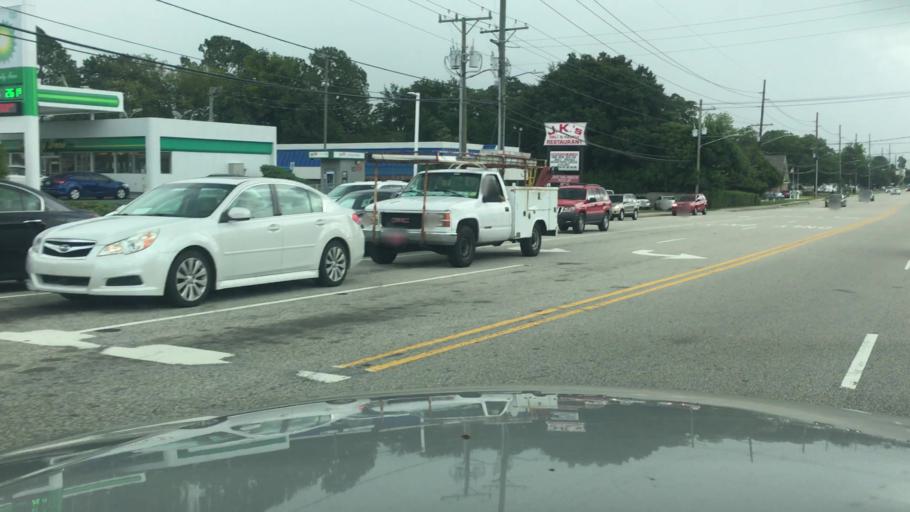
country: US
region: North Carolina
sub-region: Cumberland County
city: Fayetteville
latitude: 35.0442
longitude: -78.9350
